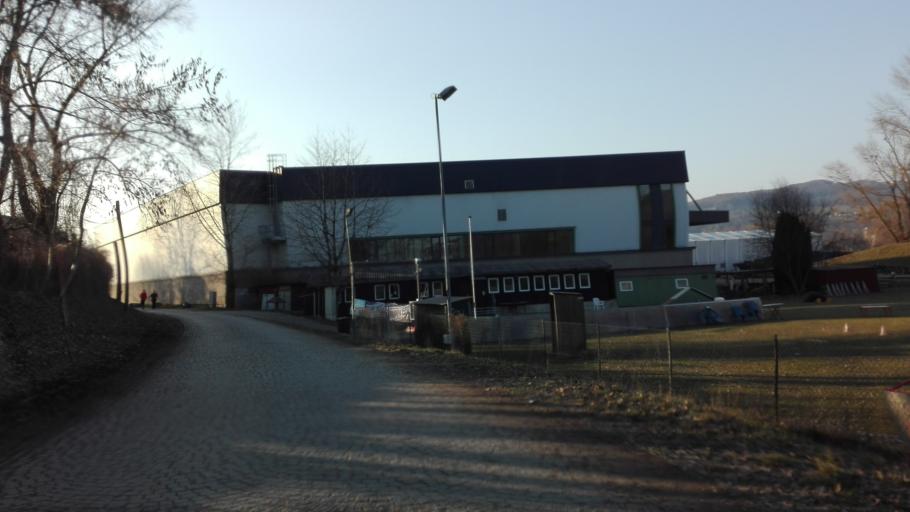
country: AT
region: Upper Austria
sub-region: Linz Stadt
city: Linz
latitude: 48.3165
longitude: 14.3197
